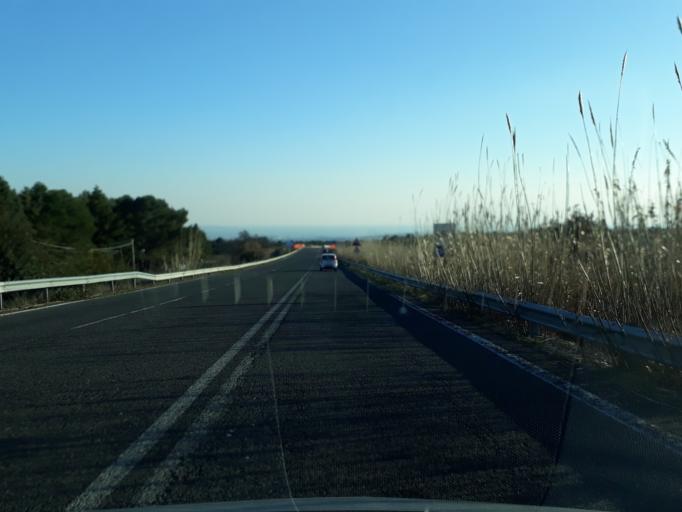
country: IT
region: Apulia
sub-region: Provincia di Taranto
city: Montemesola
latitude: 40.6291
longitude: 17.3160
